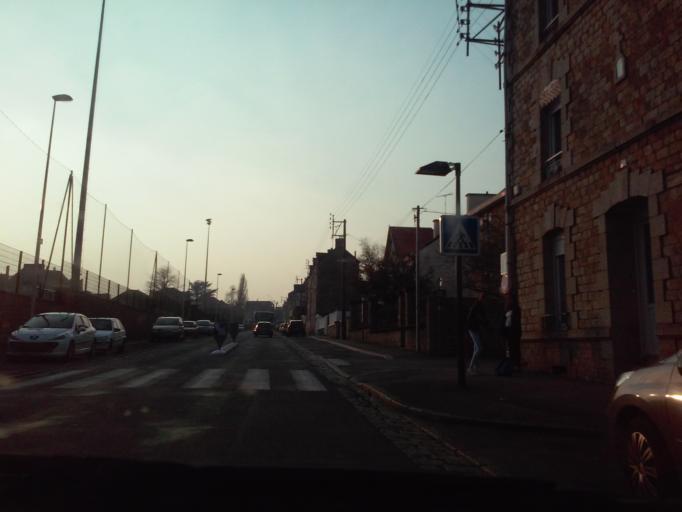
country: FR
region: Brittany
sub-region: Departement d'Ille-et-Vilaine
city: Fougeres
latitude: 48.3462
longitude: -1.1993
